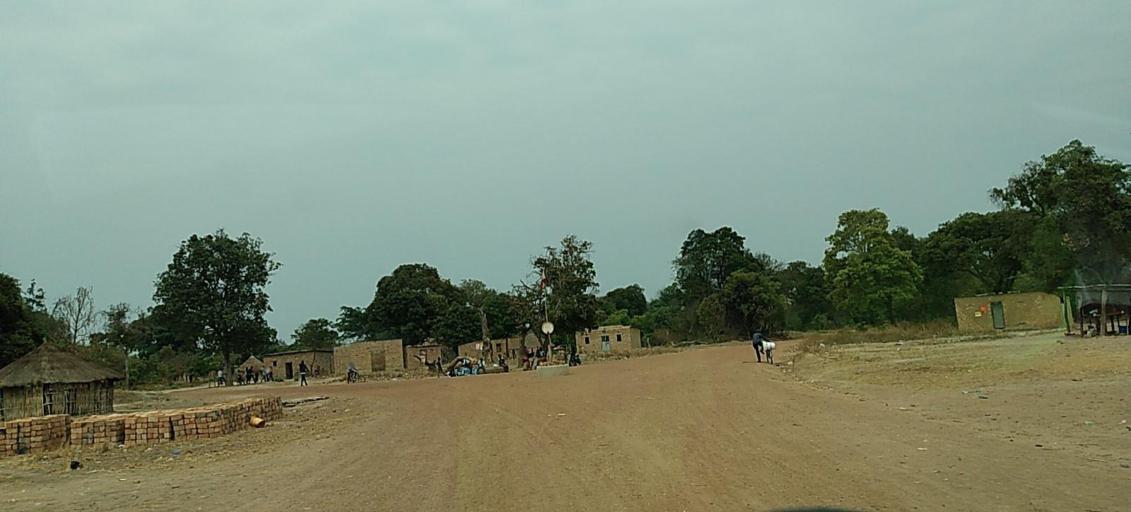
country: ZM
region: North-Western
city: Solwezi
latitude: -12.4767
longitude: 26.5279
